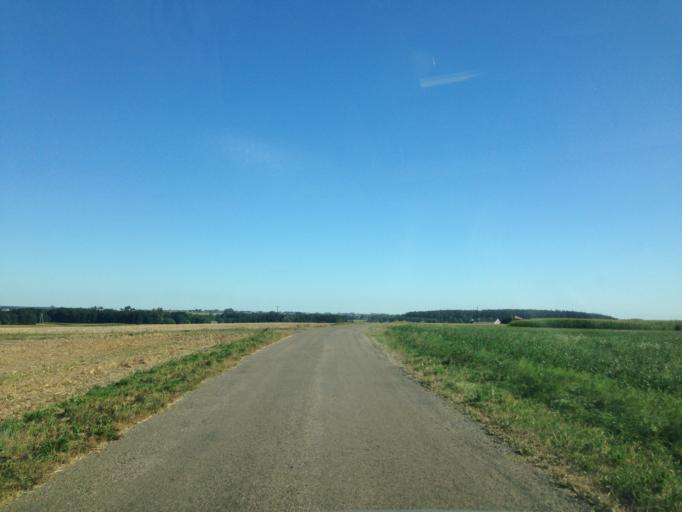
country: PL
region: Kujawsko-Pomorskie
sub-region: Powiat brodnicki
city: Swiedziebnia
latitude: 53.2030
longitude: 19.5264
